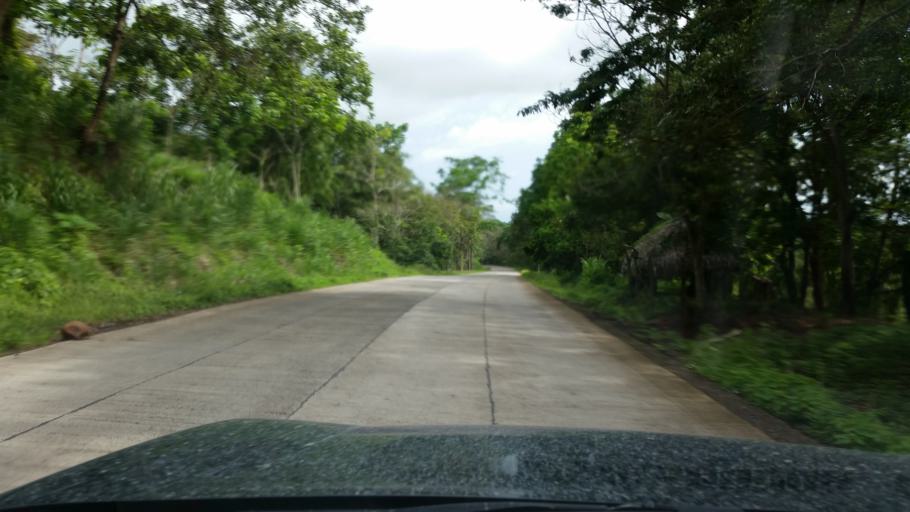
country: NI
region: Atlantico Norte (RAAN)
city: Siuna
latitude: 13.5481
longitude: -84.8213
